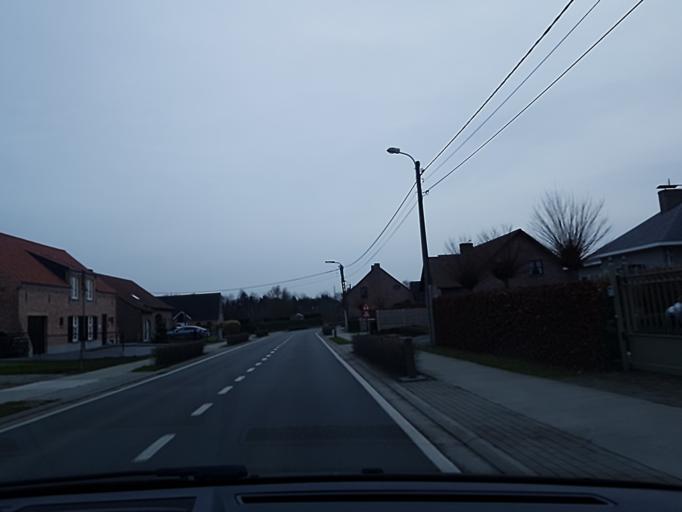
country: BE
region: Flanders
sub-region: Provincie Antwerpen
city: Putte
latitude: 51.0457
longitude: 4.6348
